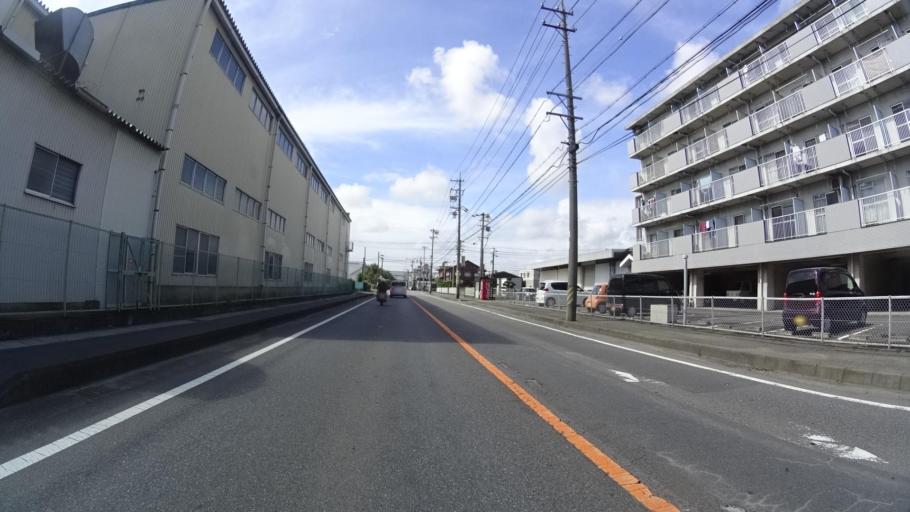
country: JP
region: Mie
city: Suzuka
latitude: 34.8691
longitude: 136.5226
